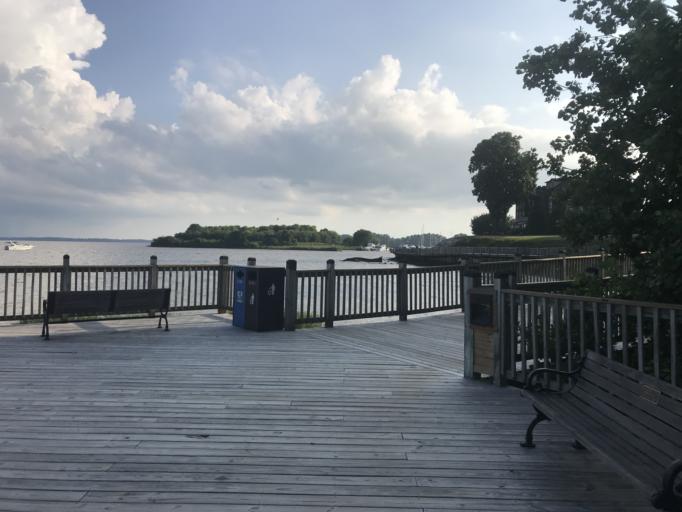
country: US
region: Maryland
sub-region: Harford County
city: Havre de Grace
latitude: 39.5395
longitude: -76.0860
